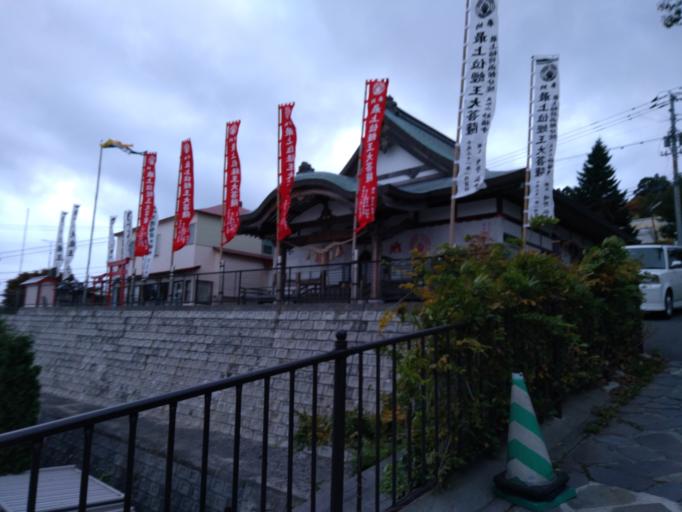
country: JP
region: Hokkaido
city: Hakodate
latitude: 41.7624
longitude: 140.7122
